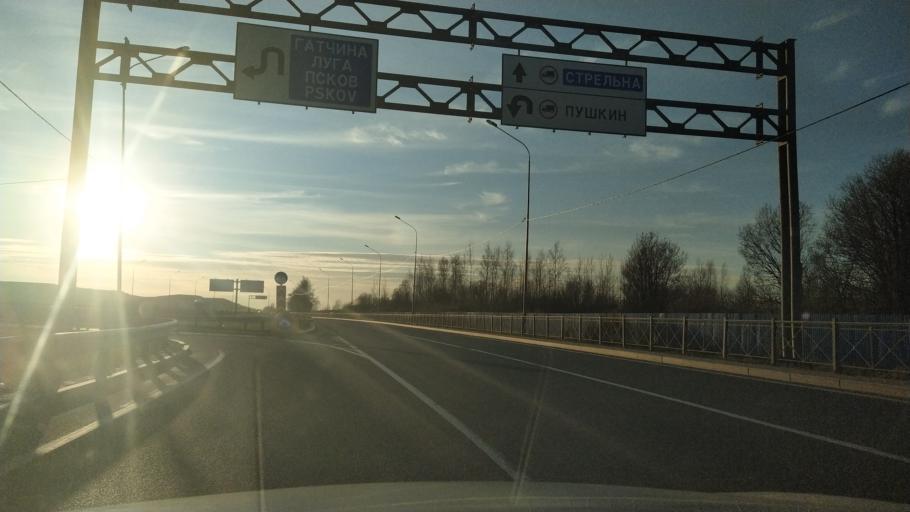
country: RU
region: St.-Petersburg
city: Aleksandrovskaya
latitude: 59.7475
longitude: 30.3020
